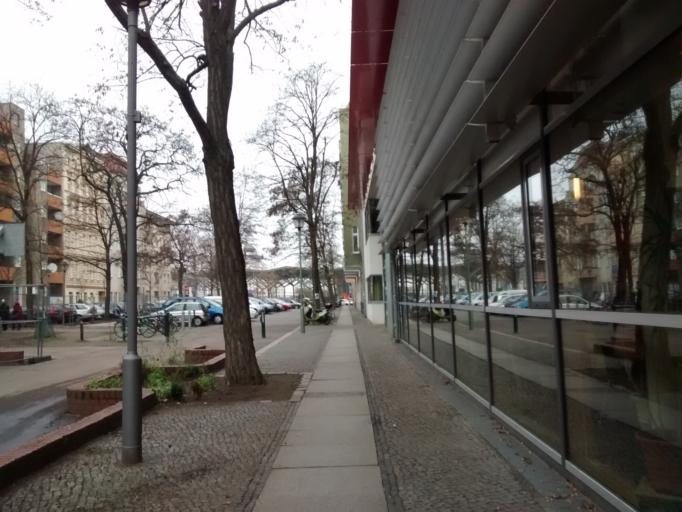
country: DE
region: Berlin
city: Moabit
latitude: 52.5315
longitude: 13.3318
